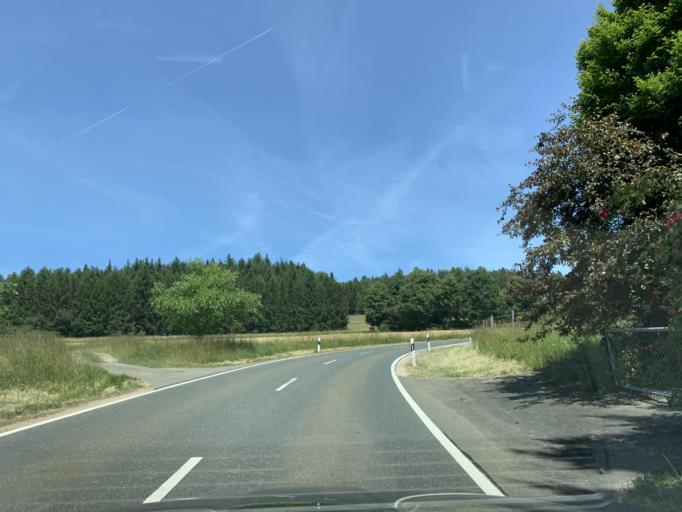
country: DE
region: Bavaria
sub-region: Upper Palatinate
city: Bach
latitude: 49.4101
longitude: 12.3625
